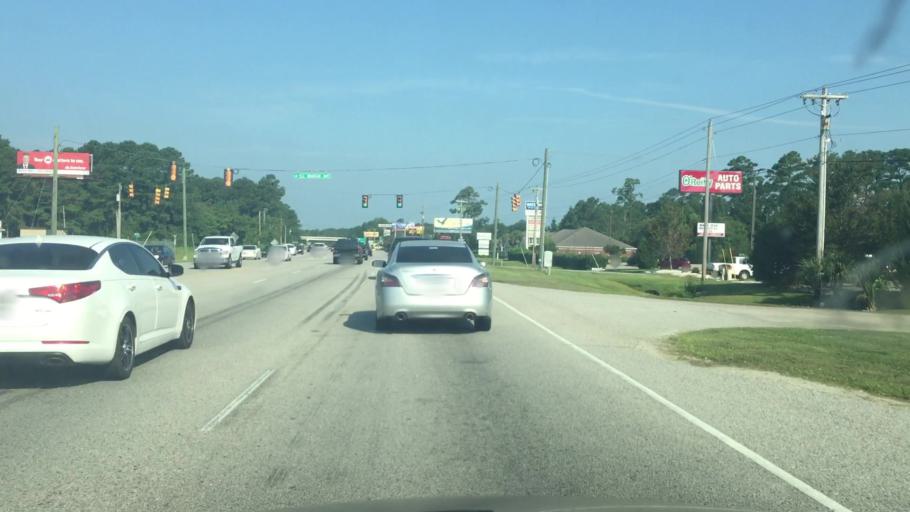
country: US
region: South Carolina
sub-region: Horry County
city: North Myrtle Beach
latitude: 33.8716
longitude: -78.6724
